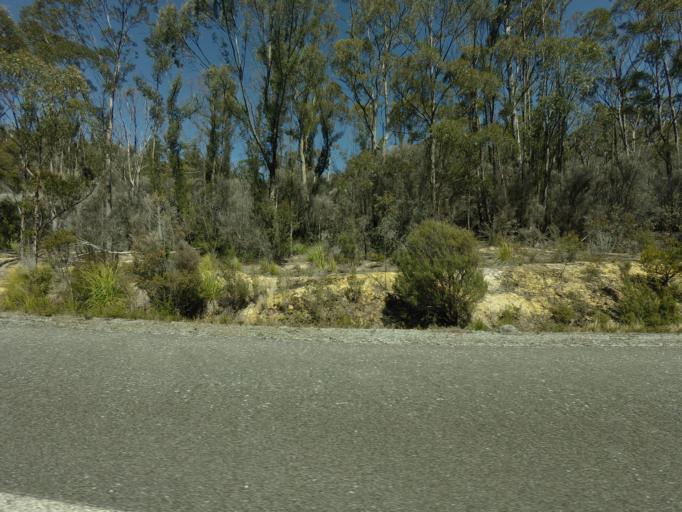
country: AU
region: Tasmania
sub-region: Huon Valley
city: Geeveston
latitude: -42.8445
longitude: 146.2497
